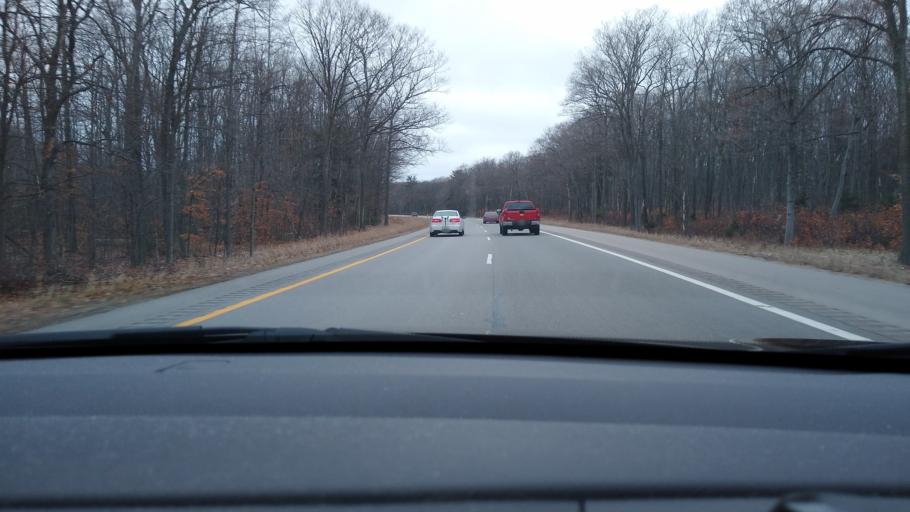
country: US
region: Michigan
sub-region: Otsego County
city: Gaylord
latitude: 44.9437
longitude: -84.6656
